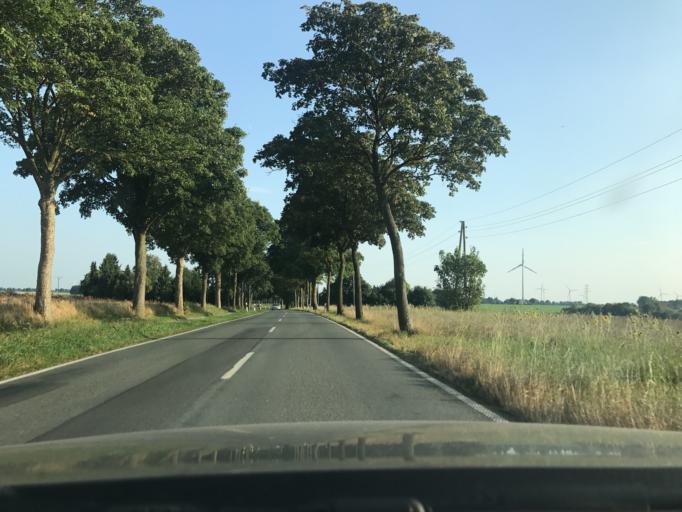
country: DE
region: North Rhine-Westphalia
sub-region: Regierungsbezirk Dusseldorf
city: Goch
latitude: 51.7366
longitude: 6.2008
